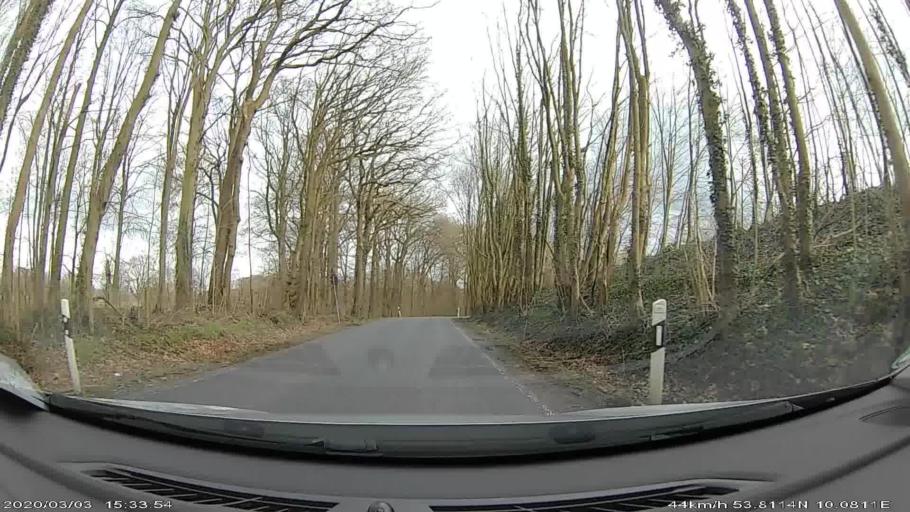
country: DE
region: Schleswig-Holstein
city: Huttblek
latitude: 53.8117
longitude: 10.0805
